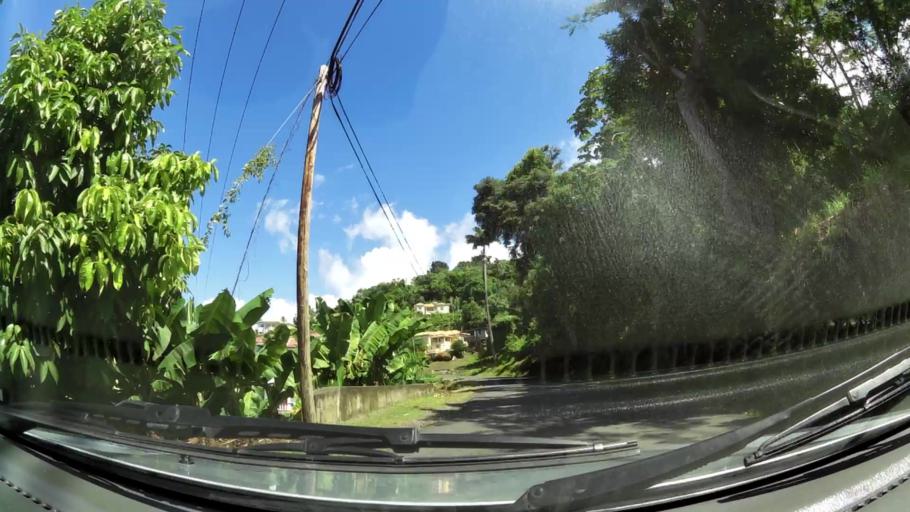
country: GD
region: Saint John
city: Gouyave
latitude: 12.1129
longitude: -61.7469
